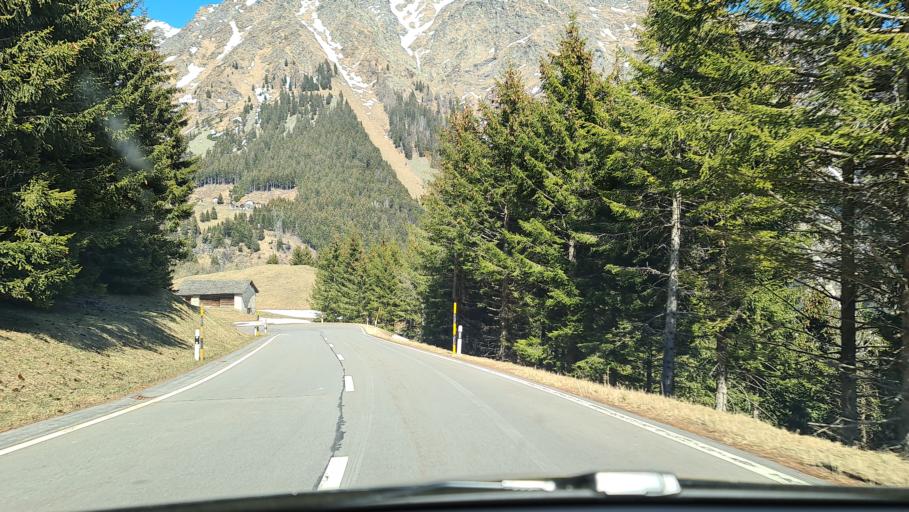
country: CH
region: Grisons
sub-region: Moesa District
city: Mesocco
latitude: 46.4354
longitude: 9.2073
